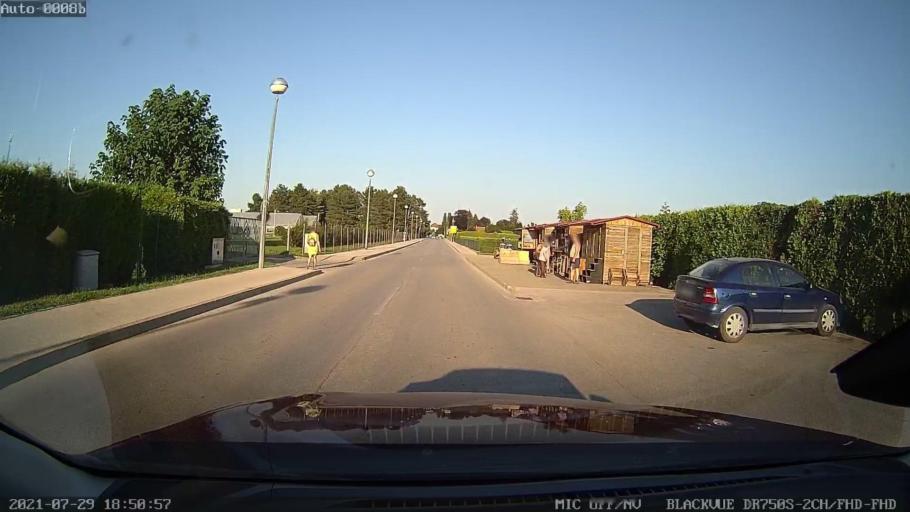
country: HR
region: Varazdinska
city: Varazdin
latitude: 46.3105
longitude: 16.3216
